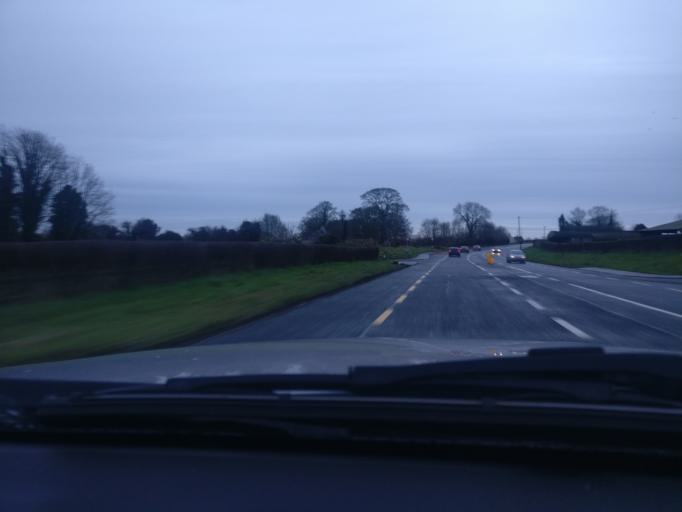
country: IE
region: Leinster
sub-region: An Mhi
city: Kells
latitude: 53.6929
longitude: -6.7835
